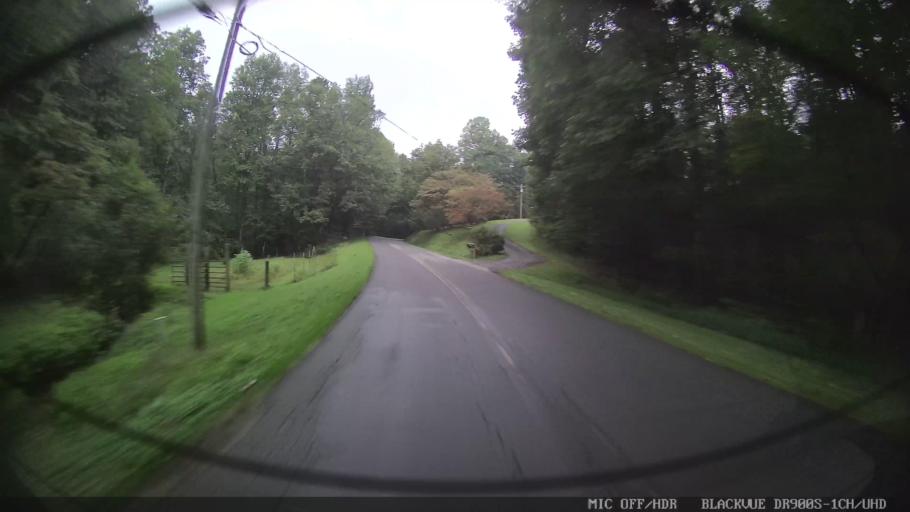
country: US
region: Georgia
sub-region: Gilmer County
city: Ellijay
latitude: 34.7580
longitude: -84.5305
